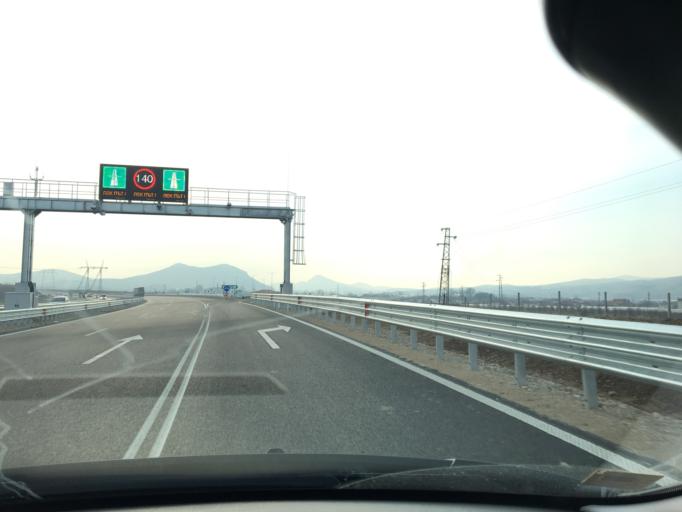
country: BG
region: Blagoevgrad
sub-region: Obshtina Sandanski
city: Sandanski
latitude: 41.5150
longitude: 23.2714
